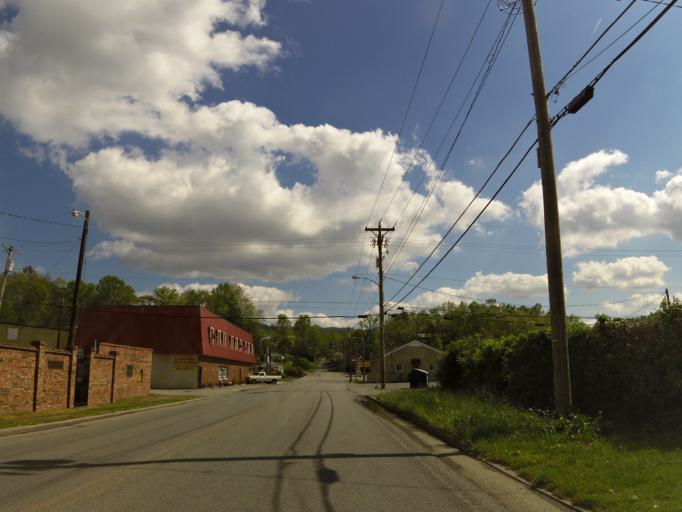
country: US
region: Kentucky
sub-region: Bell County
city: Middlesboro
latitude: 36.6089
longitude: -83.7066
